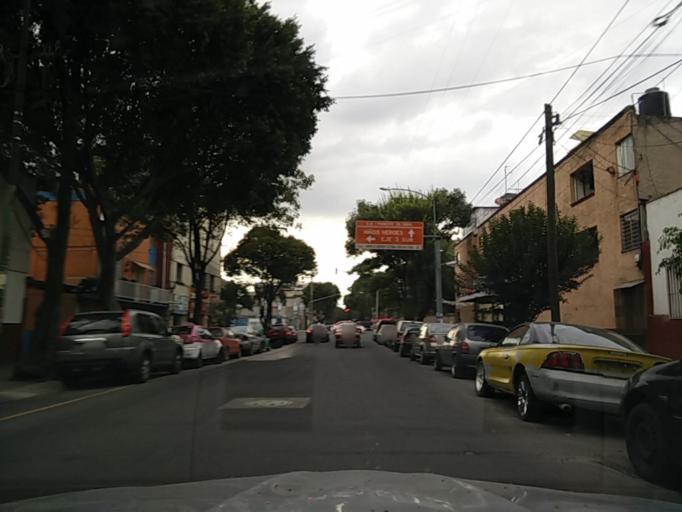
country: MX
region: Mexico City
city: Mexico City
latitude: 19.4192
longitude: -99.1468
